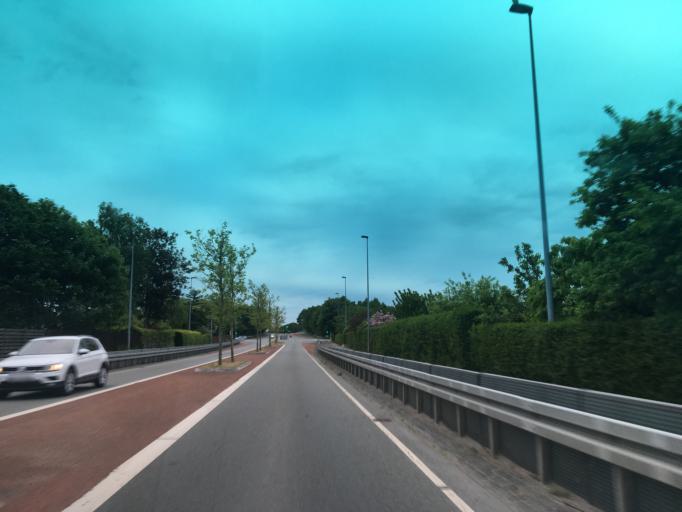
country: DK
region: Capital Region
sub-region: Albertslund Kommune
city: Albertslund
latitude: 55.6450
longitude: 12.3558
